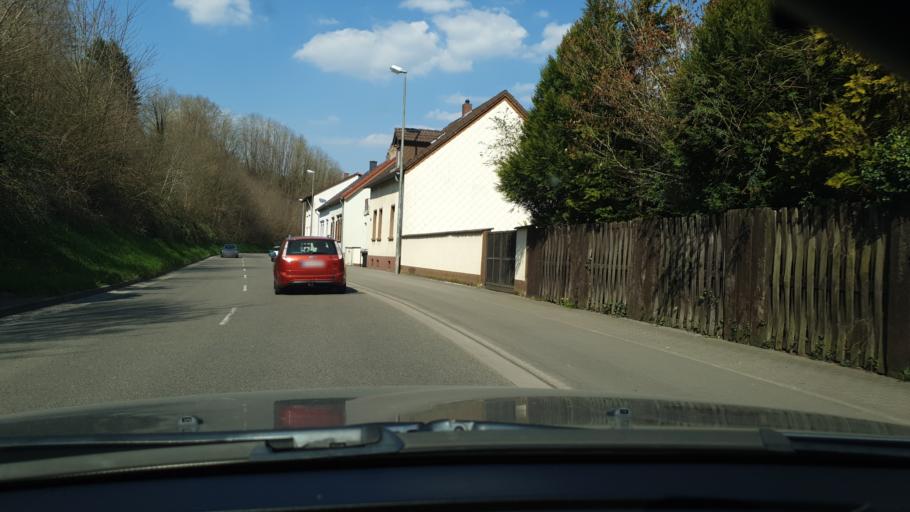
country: DE
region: Rheinland-Pfalz
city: Zweibrucken
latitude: 49.2585
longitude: 7.3978
